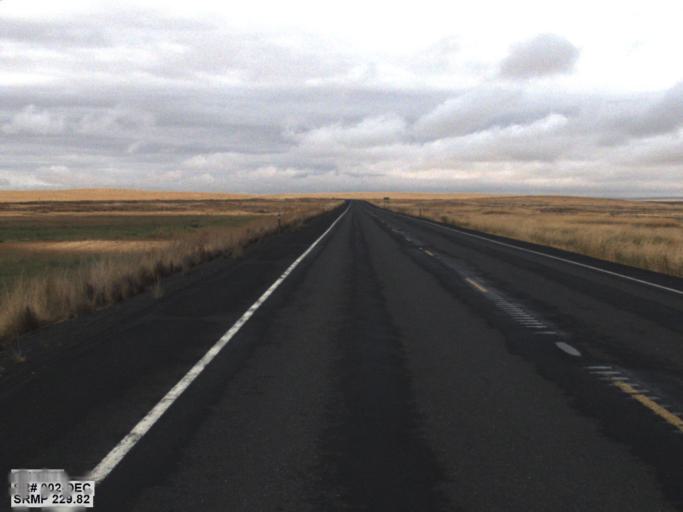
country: US
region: Washington
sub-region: Lincoln County
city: Davenport
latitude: 47.7603
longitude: -118.5335
